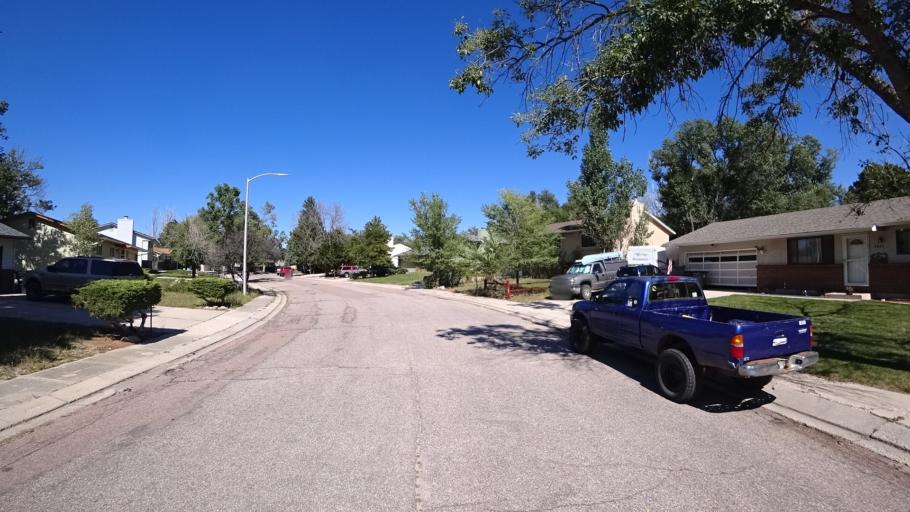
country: US
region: Colorado
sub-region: El Paso County
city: Cimarron Hills
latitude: 38.8778
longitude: -104.7381
